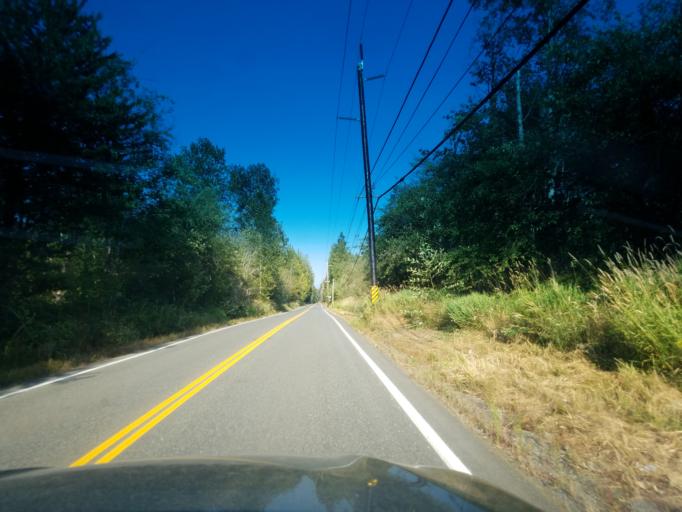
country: US
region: Washington
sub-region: King County
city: Union Hill-Novelty Hill
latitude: 47.6572
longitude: -121.9993
